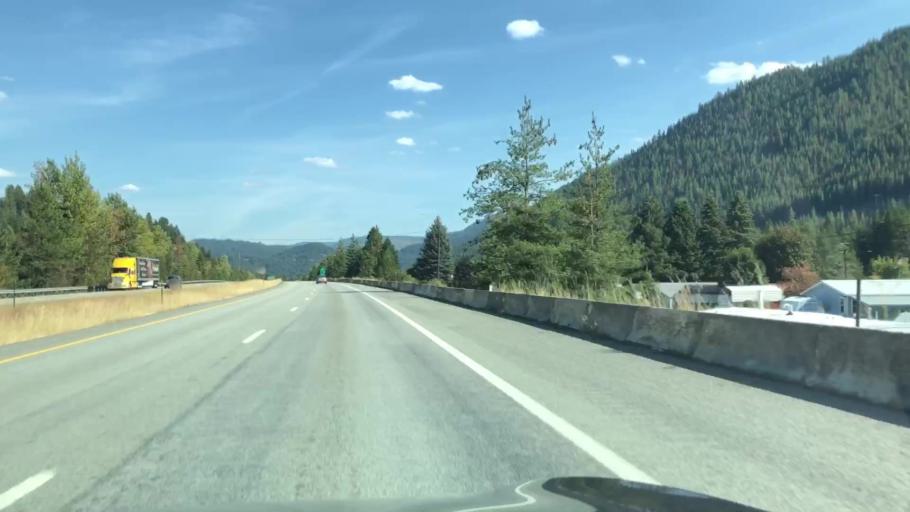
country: US
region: Idaho
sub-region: Shoshone County
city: Osburn
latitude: 47.5146
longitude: -116.0294
